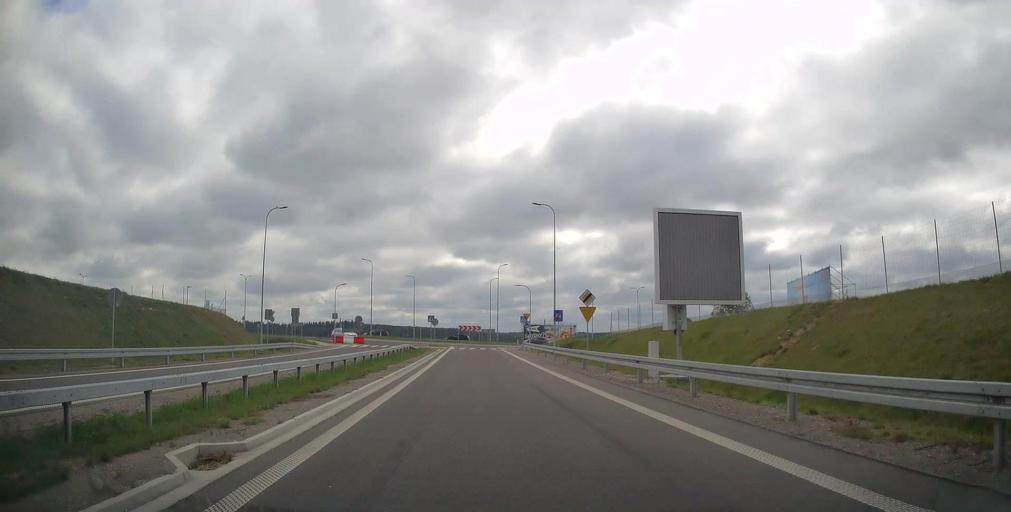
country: PL
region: Lesser Poland Voivodeship
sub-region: Powiat krakowski
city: Michalowice
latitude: 50.2071
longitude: 20.0152
